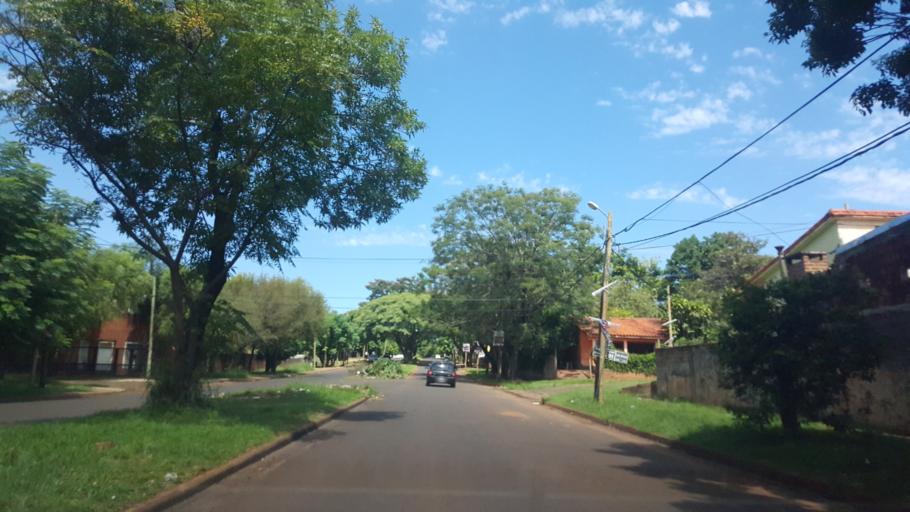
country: AR
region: Misiones
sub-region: Departamento de Capital
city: Posadas
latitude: -27.3765
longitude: -55.9217
